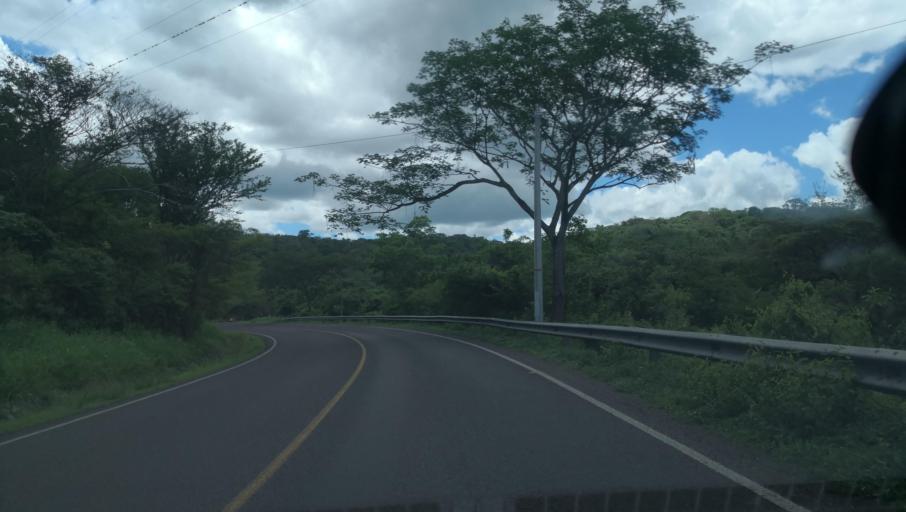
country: NI
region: Madriz
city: Palacaguina
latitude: 13.4347
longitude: -86.4275
